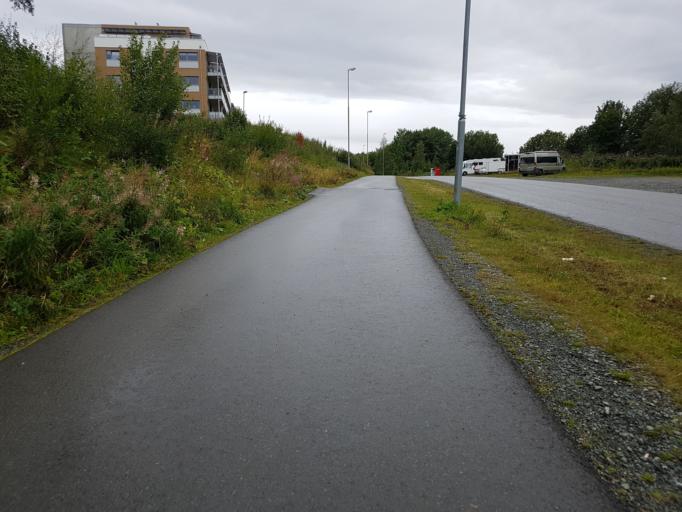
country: NO
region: Sor-Trondelag
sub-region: Trondheim
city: Trondheim
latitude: 63.4095
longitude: 10.4807
